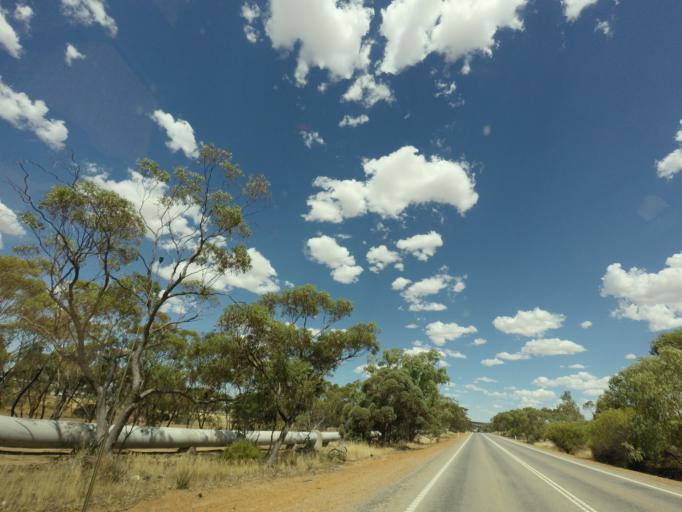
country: AU
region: Western Australia
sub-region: Cunderdin
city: Cunderdin
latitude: -31.6448
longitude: 117.1941
